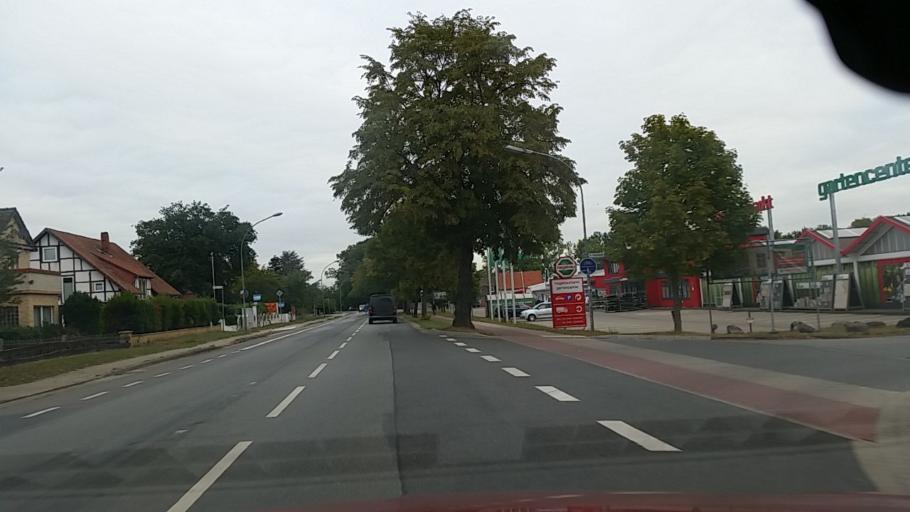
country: DE
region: Lower Saxony
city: Gifhorn
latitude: 52.5001
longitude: 10.5420
